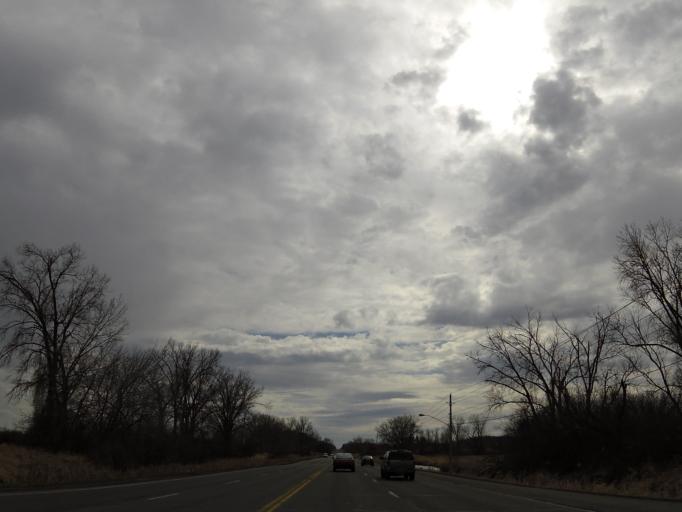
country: US
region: Minnesota
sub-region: Hennepin County
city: Bloomington
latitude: 44.8389
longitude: -93.3294
